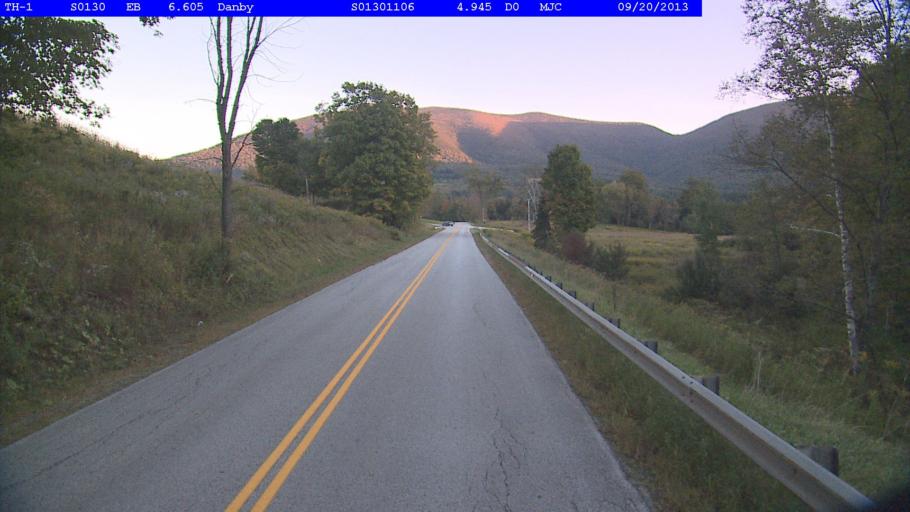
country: US
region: Vermont
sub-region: Bennington County
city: Manchester Center
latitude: 43.3449
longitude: -73.0463
